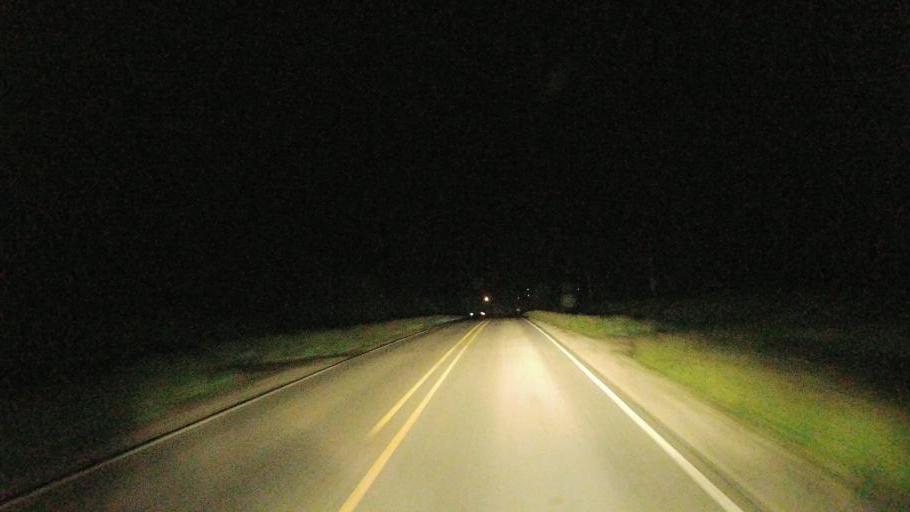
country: US
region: Iowa
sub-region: Decatur County
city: Lamoni
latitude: 40.6239
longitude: -94.0020
